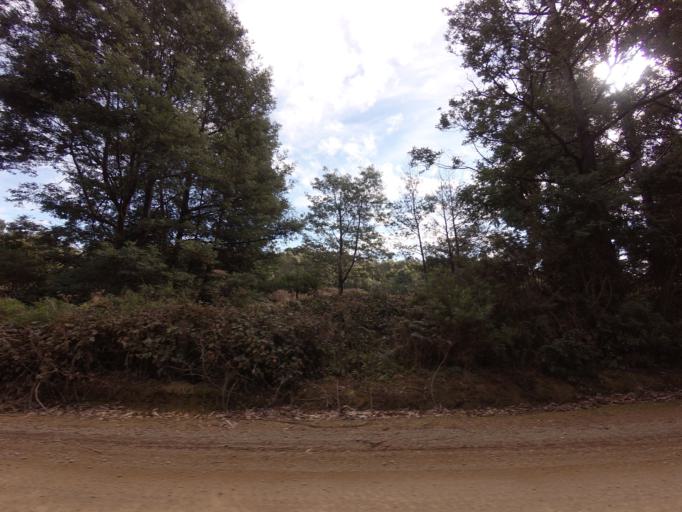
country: AU
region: Tasmania
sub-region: Clarence
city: Sandford
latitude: -43.1445
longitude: 147.7640
